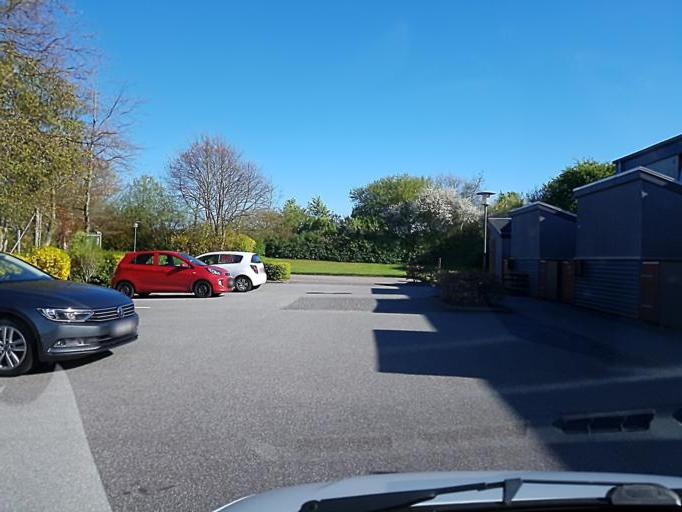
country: DK
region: South Denmark
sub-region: Esbjerg Kommune
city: Esbjerg
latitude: 55.5126
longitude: 8.4473
